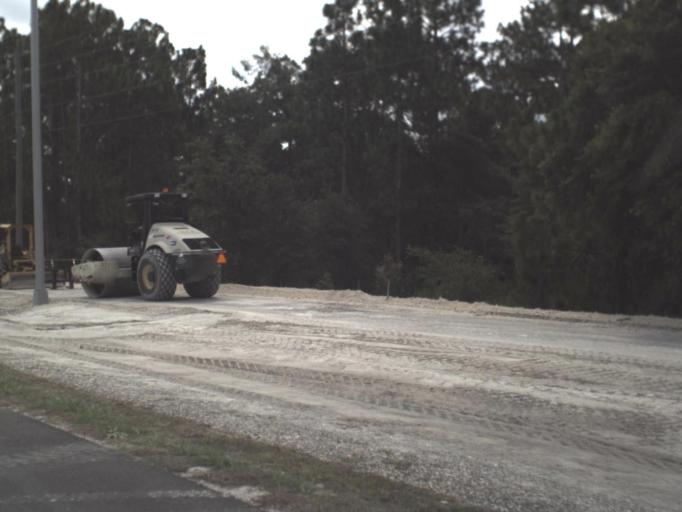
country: US
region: Florida
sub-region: Hernando County
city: High Point
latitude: 28.5322
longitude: -82.5399
